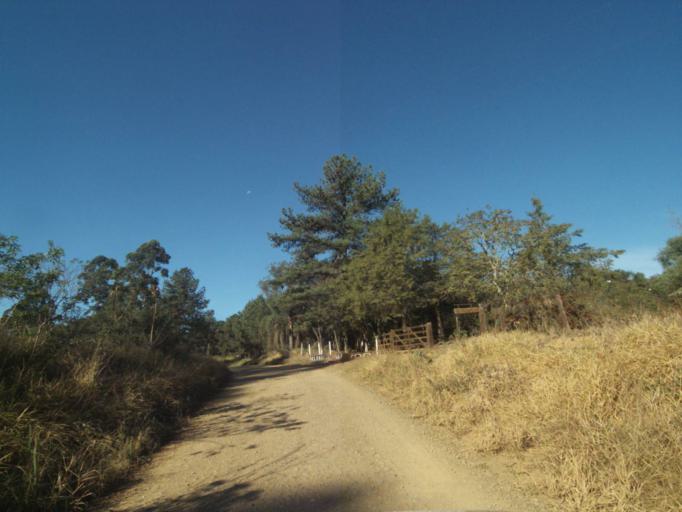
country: BR
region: Parana
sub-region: Tibagi
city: Tibagi
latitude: -24.5448
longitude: -50.5097
